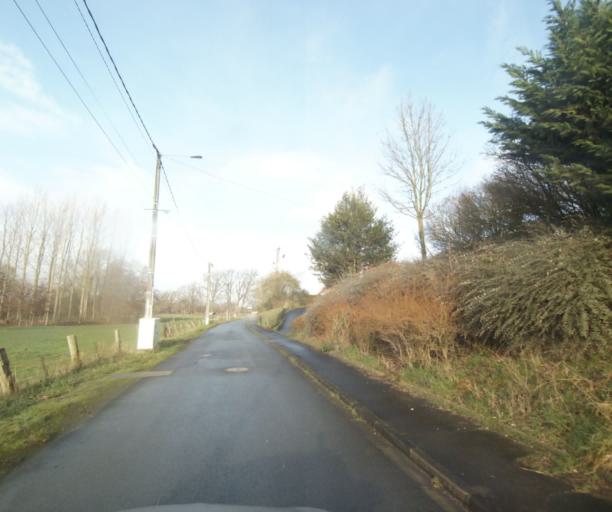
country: FR
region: Nord-Pas-de-Calais
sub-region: Departement du Nord
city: Thiant
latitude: 50.2899
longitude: 3.4542
